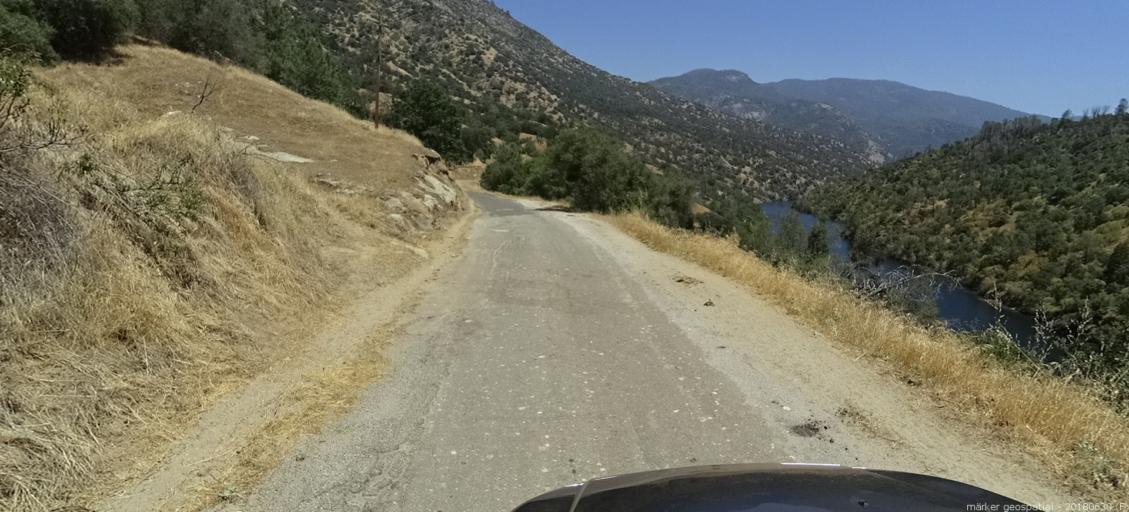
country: US
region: California
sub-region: Fresno County
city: Auberry
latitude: 37.1653
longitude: -119.4200
